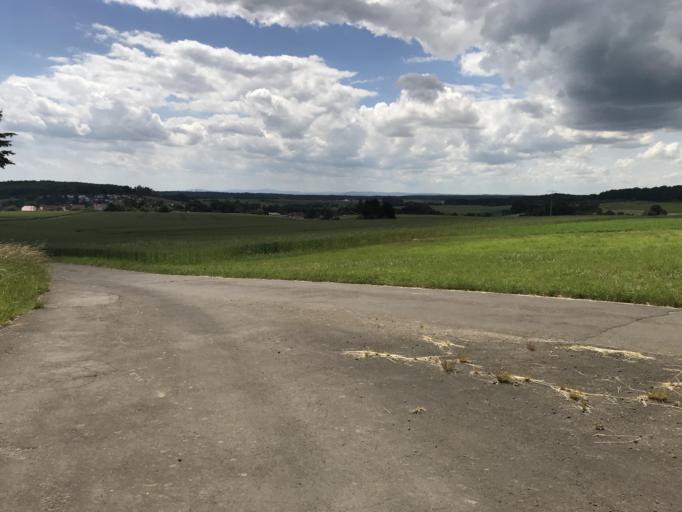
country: DE
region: Hesse
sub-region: Regierungsbezirk Giessen
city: Grunberg
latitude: 50.5840
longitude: 8.9374
